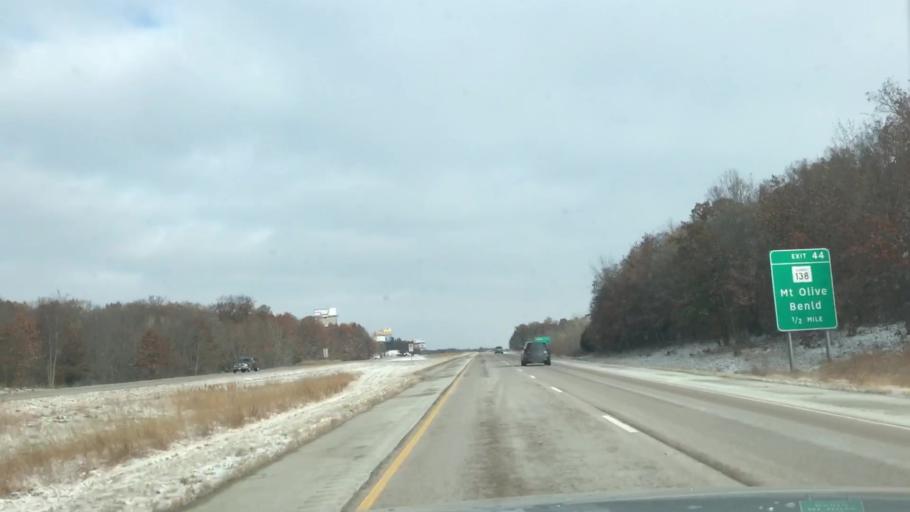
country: US
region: Illinois
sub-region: Macoupin County
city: Mount Olive
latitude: 39.0607
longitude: -89.7556
